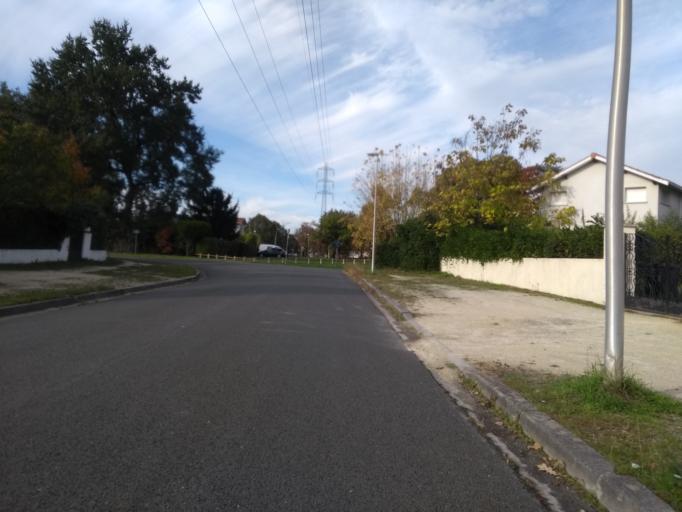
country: FR
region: Aquitaine
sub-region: Departement de la Gironde
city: Pessac
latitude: 44.7933
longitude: -0.6737
